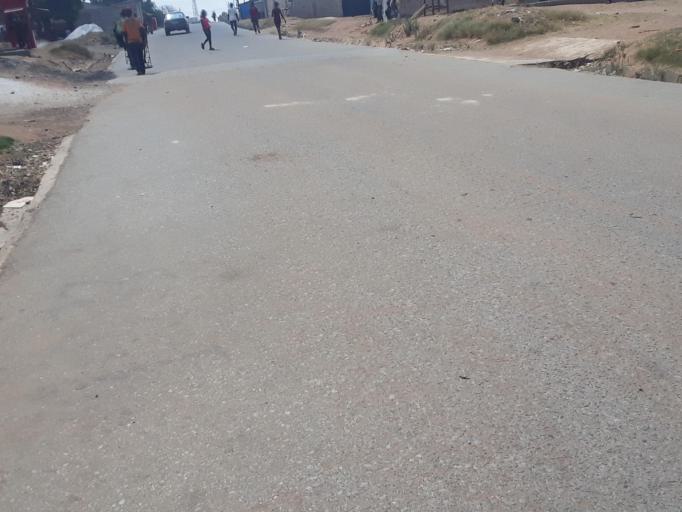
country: ZM
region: Lusaka
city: Lusaka
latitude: -15.3613
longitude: 28.3031
